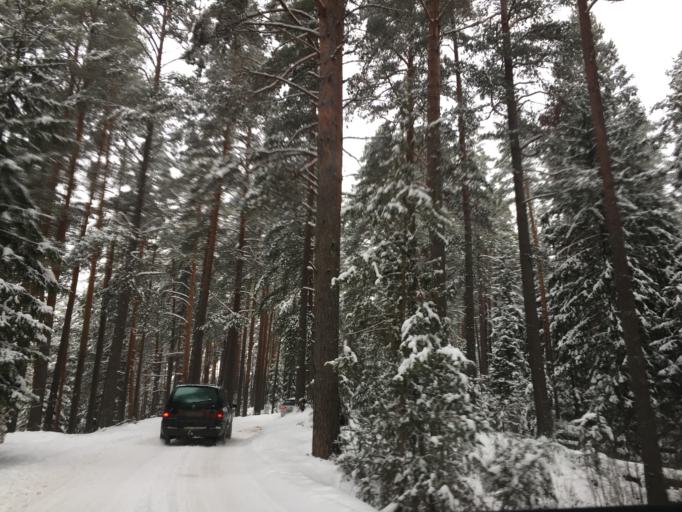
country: LV
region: Smiltene
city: Smiltene
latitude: 57.4022
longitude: 25.9485
